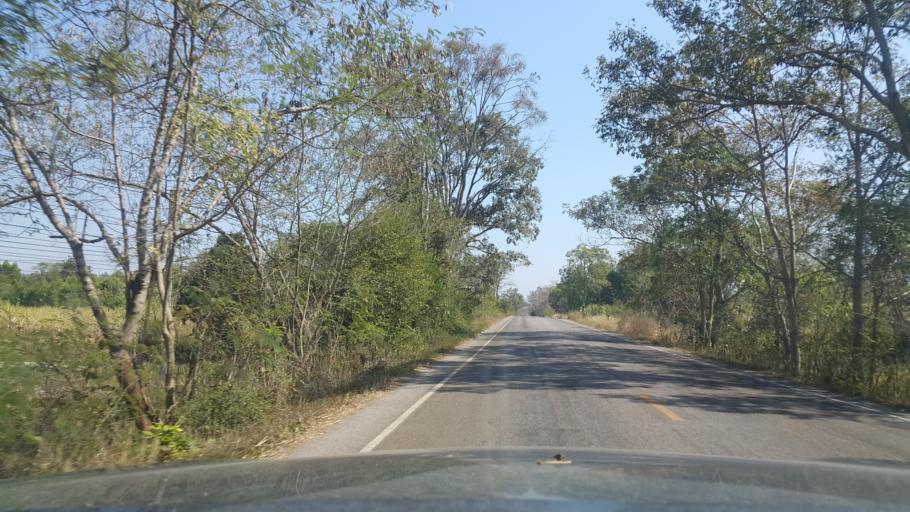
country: TH
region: Changwat Udon Thani
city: Ban Dung
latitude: 17.6092
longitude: 103.3057
